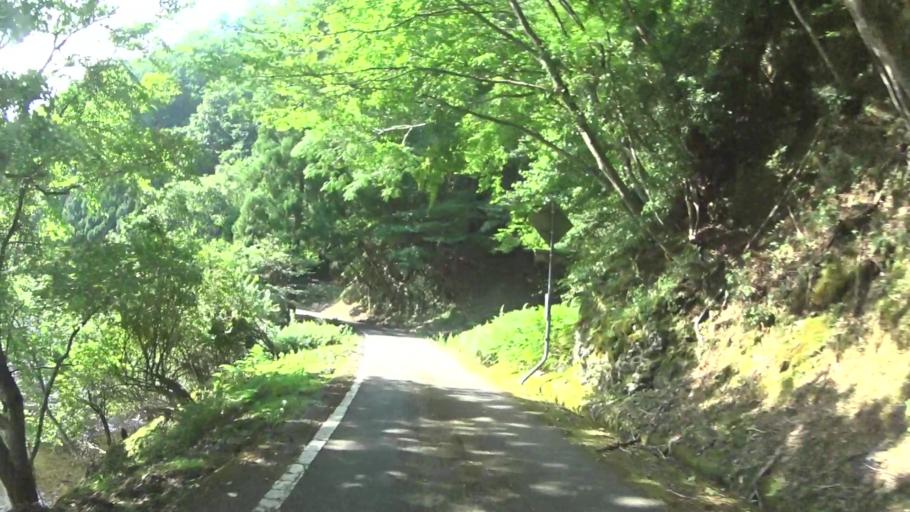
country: JP
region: Fukui
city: Obama
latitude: 35.2716
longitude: 135.6937
